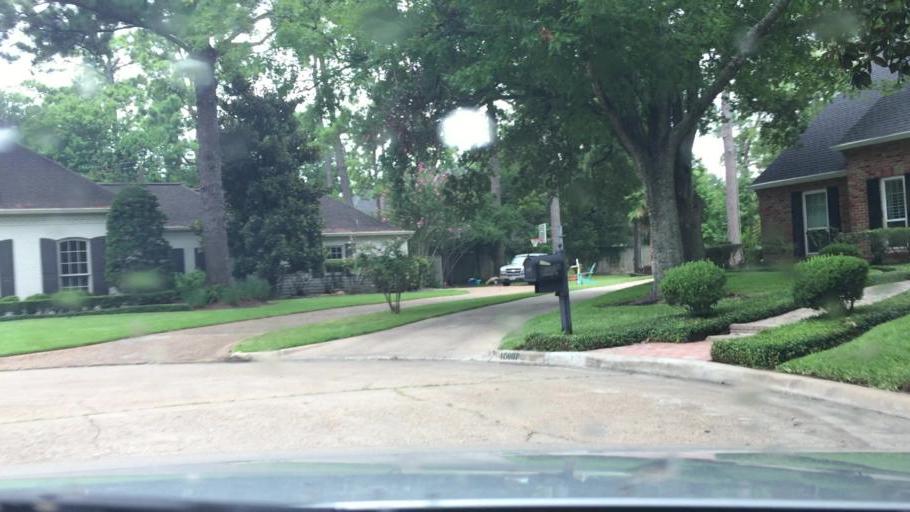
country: US
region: Texas
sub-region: Harris County
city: Hunters Creek Village
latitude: 29.7676
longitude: -95.5024
